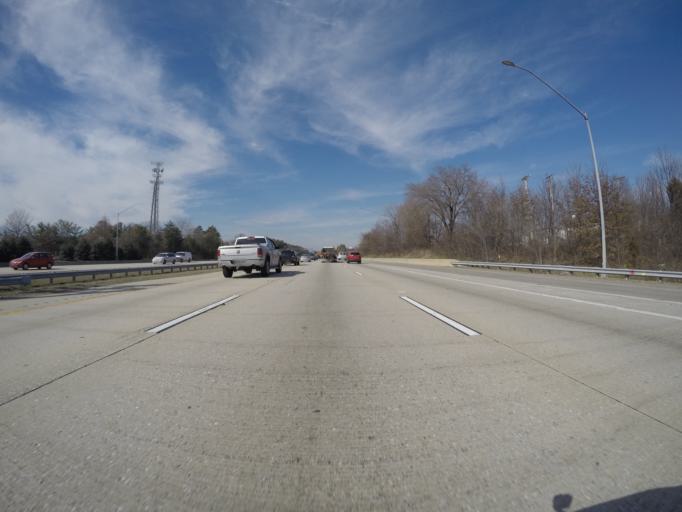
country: US
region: Maryland
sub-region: Anne Arundel County
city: South Gate
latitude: 39.0971
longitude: -76.6274
